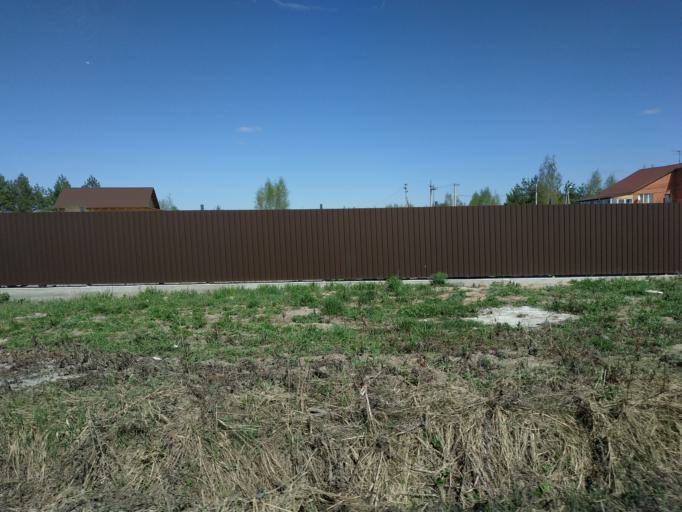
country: RU
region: Moskovskaya
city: Malyshevo
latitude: 55.4605
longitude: 38.3656
